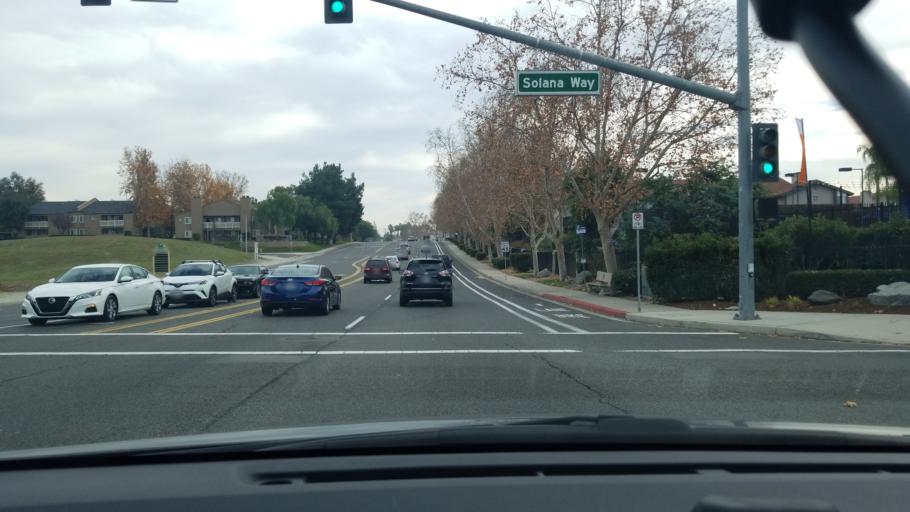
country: US
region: California
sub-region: Riverside County
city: Temecula
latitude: 33.5162
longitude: -117.1500
